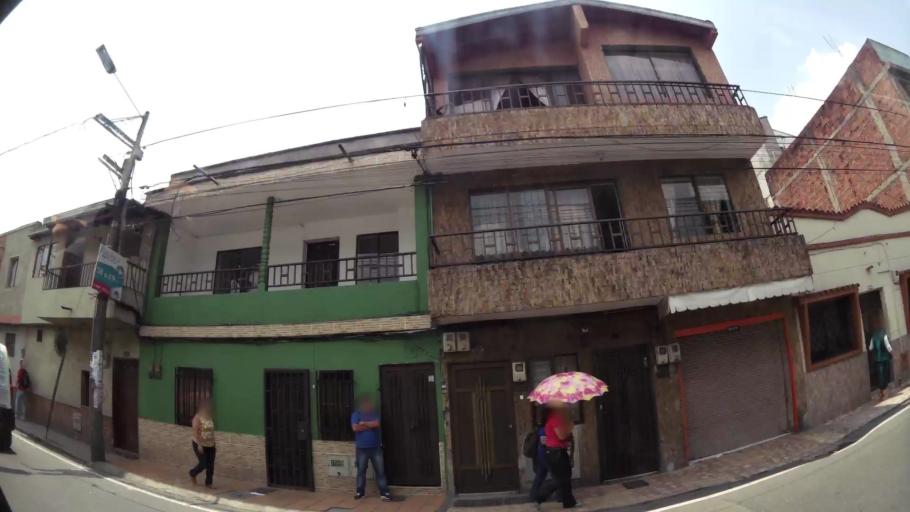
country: CO
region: Antioquia
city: Sabaneta
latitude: 6.1710
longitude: -75.6135
